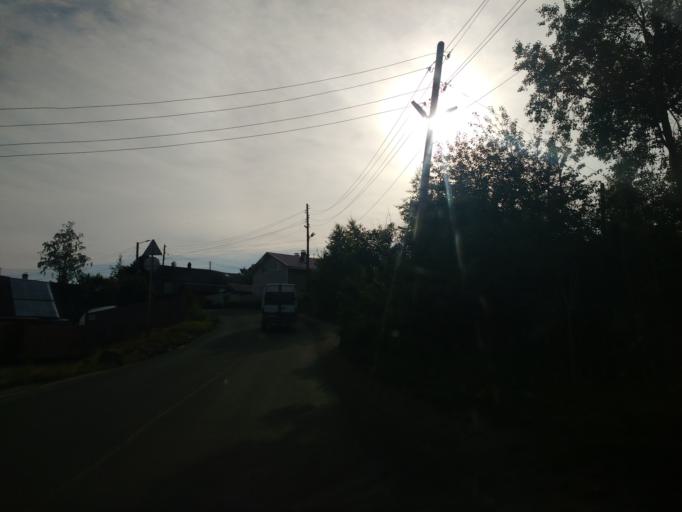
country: RU
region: Republic of Karelia
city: Petrozavodsk
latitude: 61.8466
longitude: 34.3551
